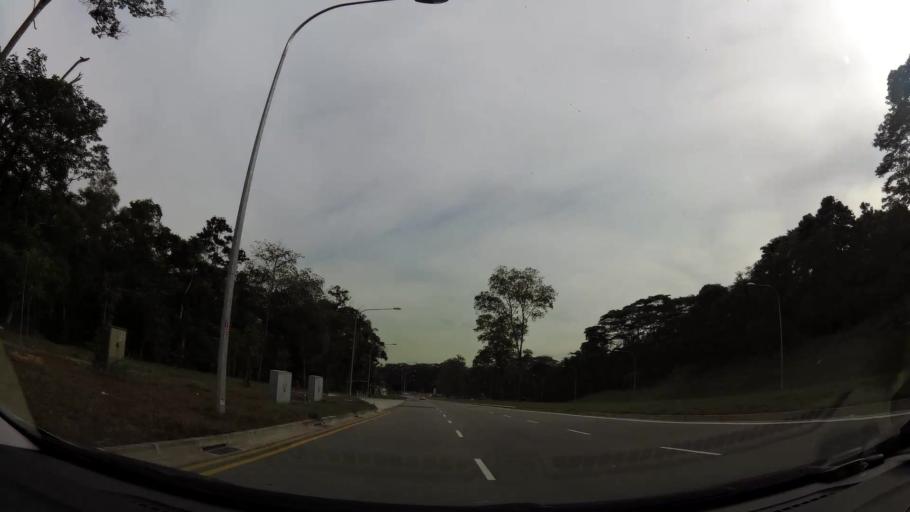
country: MY
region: Johor
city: Johor Bahru
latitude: 1.3605
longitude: 103.6938
